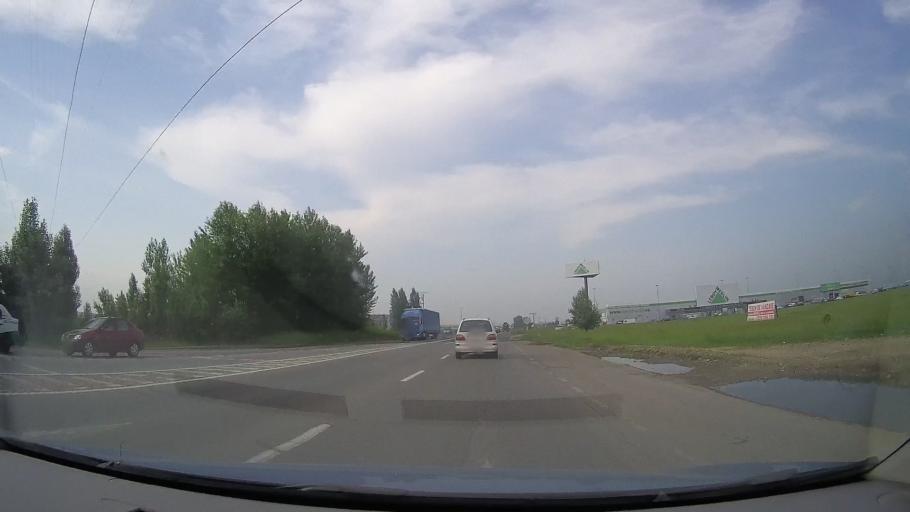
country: RO
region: Timis
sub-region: Comuna Giroc
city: Chisoda
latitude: 45.7052
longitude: 21.1859
